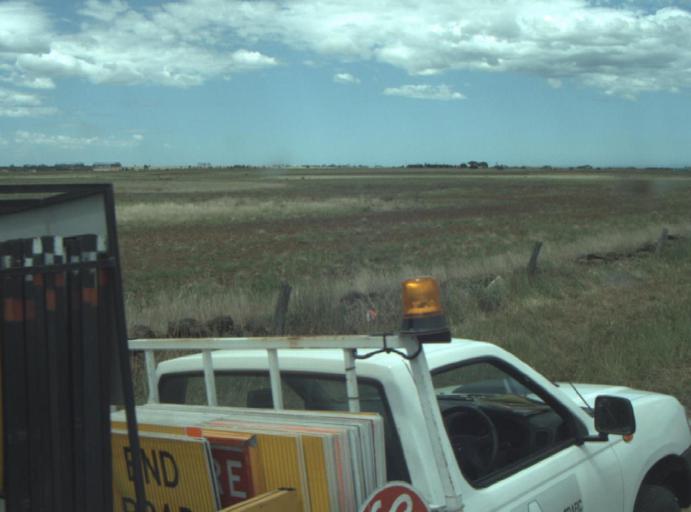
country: AU
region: Victoria
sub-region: Wyndham
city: Little River
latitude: -37.8917
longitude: 144.4619
